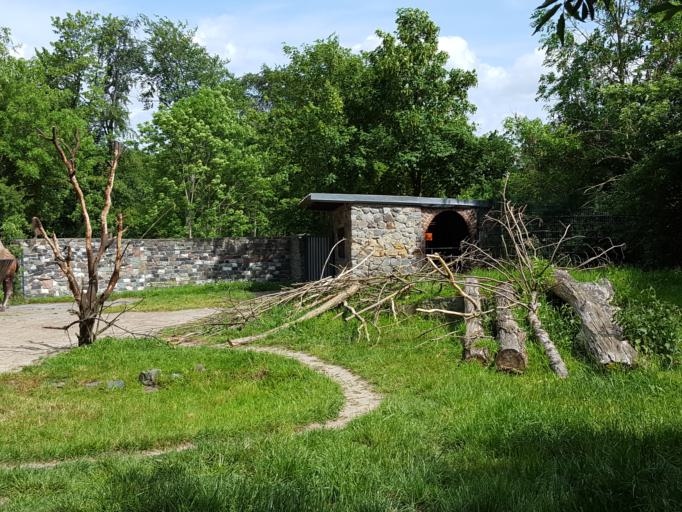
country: DE
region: North Rhine-Westphalia
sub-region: Regierungsbezirk Arnsberg
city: Hamm
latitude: 51.6606
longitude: 7.8150
